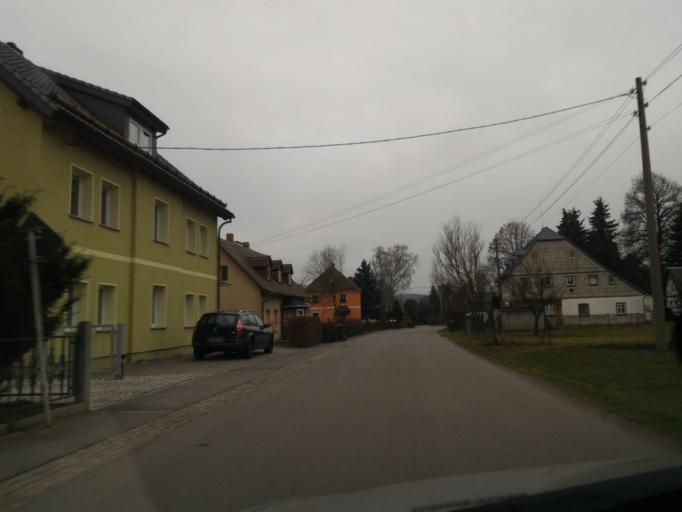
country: DE
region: Saxony
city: Leutersdorf
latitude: 50.9560
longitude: 14.6479
